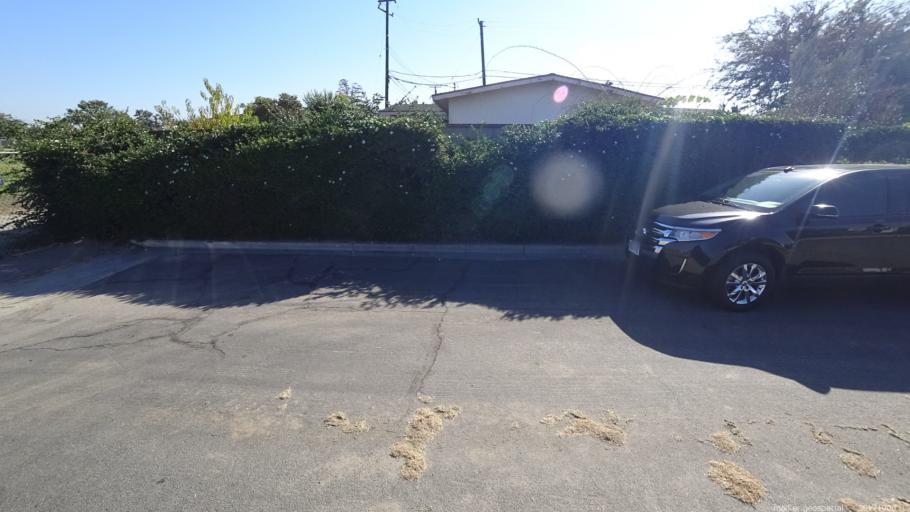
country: US
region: California
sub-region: Orange County
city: Stanton
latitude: 33.7870
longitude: -117.9791
